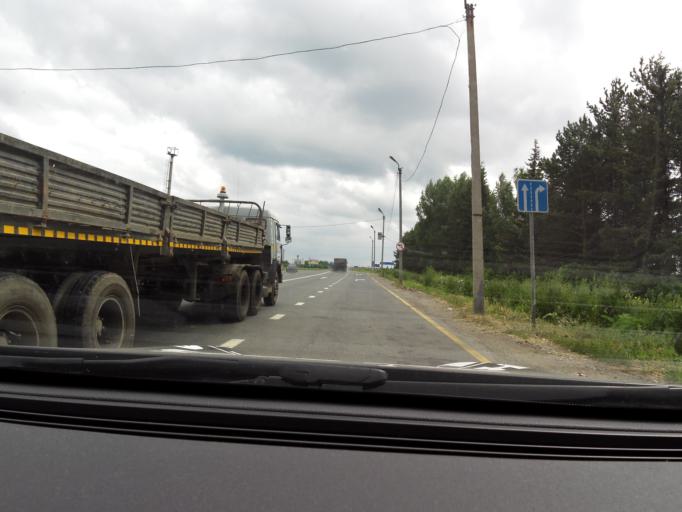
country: RU
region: Perm
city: Kungur
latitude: 57.4081
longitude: 56.8784
